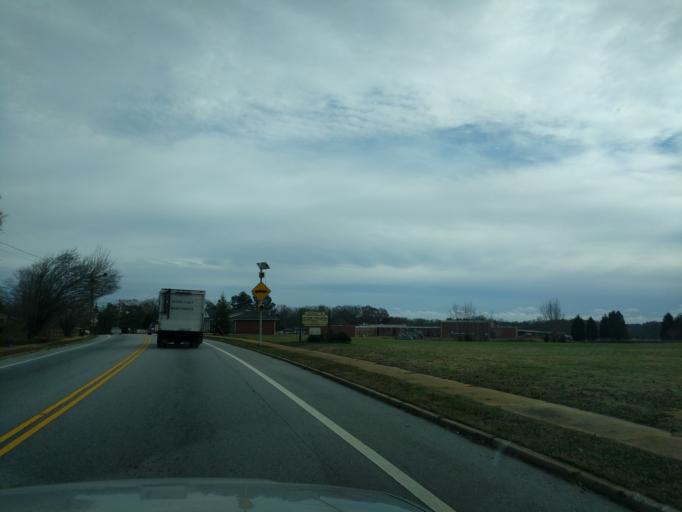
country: US
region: South Carolina
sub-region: Anderson County
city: Williamston
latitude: 34.6487
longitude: -82.4837
